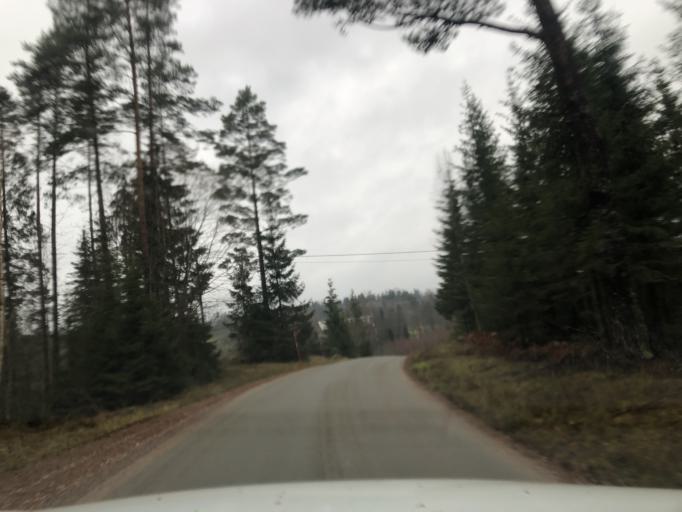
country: SE
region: Vaestra Goetaland
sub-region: Ulricehamns Kommun
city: Ulricehamn
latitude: 57.8560
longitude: 13.6267
